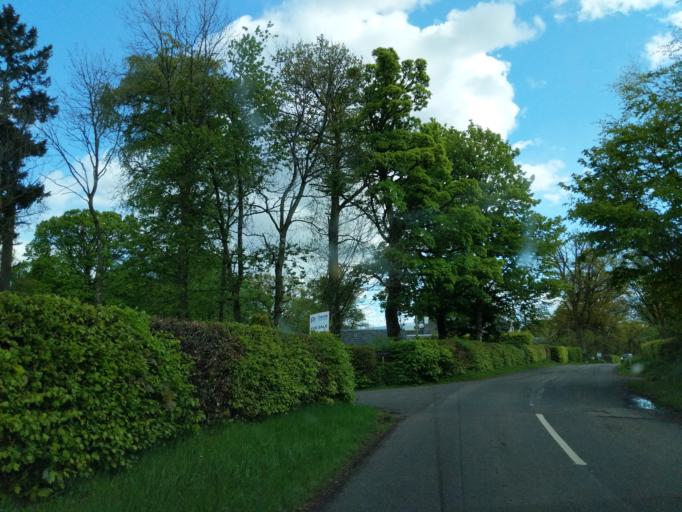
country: GB
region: Scotland
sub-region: Stirling
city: Callander
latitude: 56.1536
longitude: -4.2602
